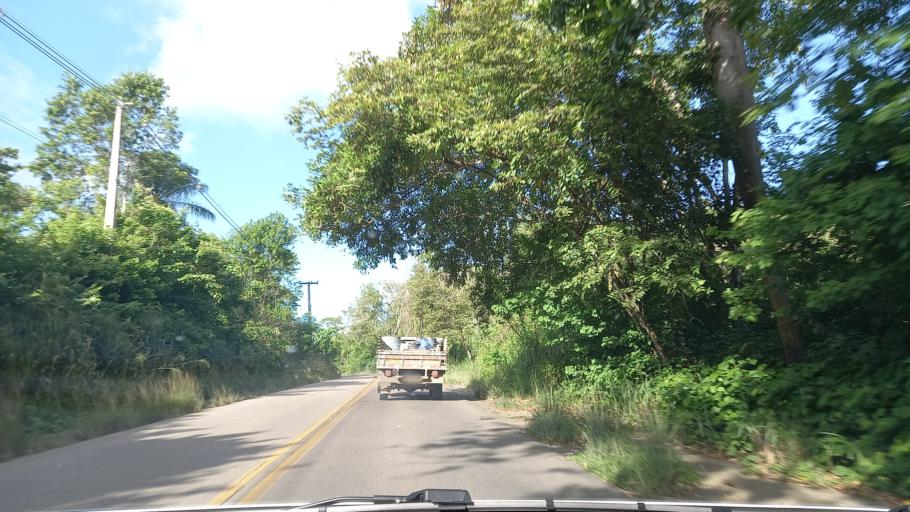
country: BR
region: Pernambuco
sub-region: Rio Formoso
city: Rio Formoso
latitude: -8.6563
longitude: -35.1390
